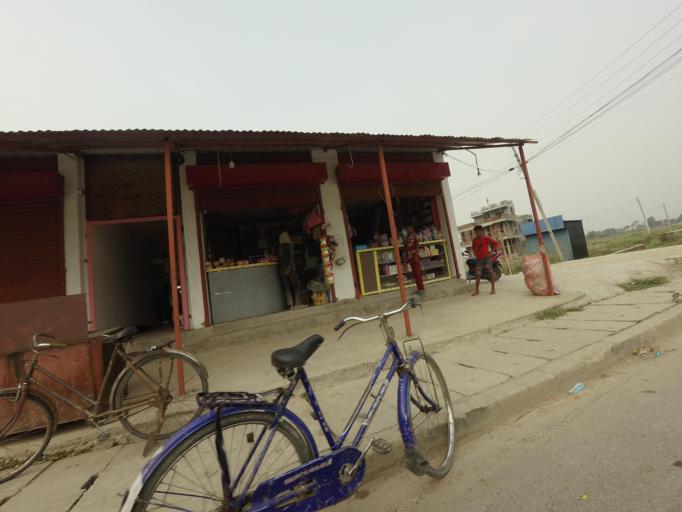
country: NP
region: Western Region
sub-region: Lumbini Zone
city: Bhairahawa
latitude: 27.5259
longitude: 83.4506
